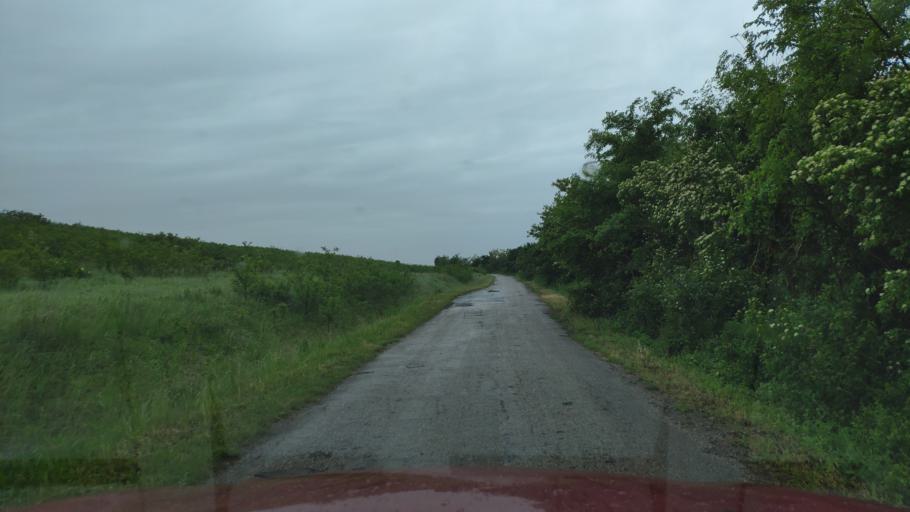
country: HU
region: Borsod-Abauj-Zemplen
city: Satoraljaujhely
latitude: 48.4275
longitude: 21.6974
